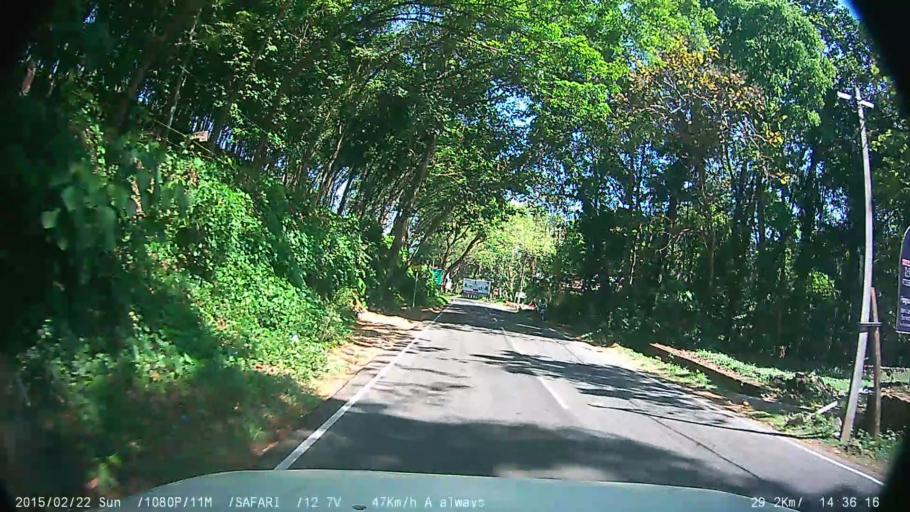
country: IN
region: Kerala
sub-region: Kottayam
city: Erattupetta
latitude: 9.5543
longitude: 76.7869
